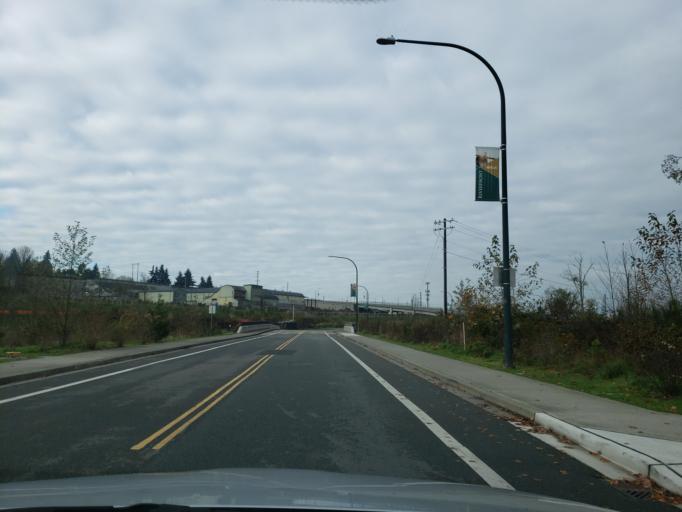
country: US
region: Washington
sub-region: Snohomish County
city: Everett
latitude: 47.9606
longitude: -122.1923
